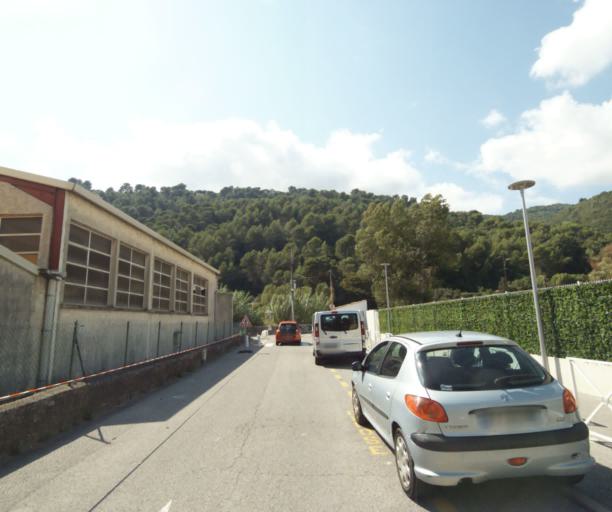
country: FR
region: Provence-Alpes-Cote d'Azur
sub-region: Departement des Alpes-Maritimes
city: Drap
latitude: 43.7571
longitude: 7.3197
